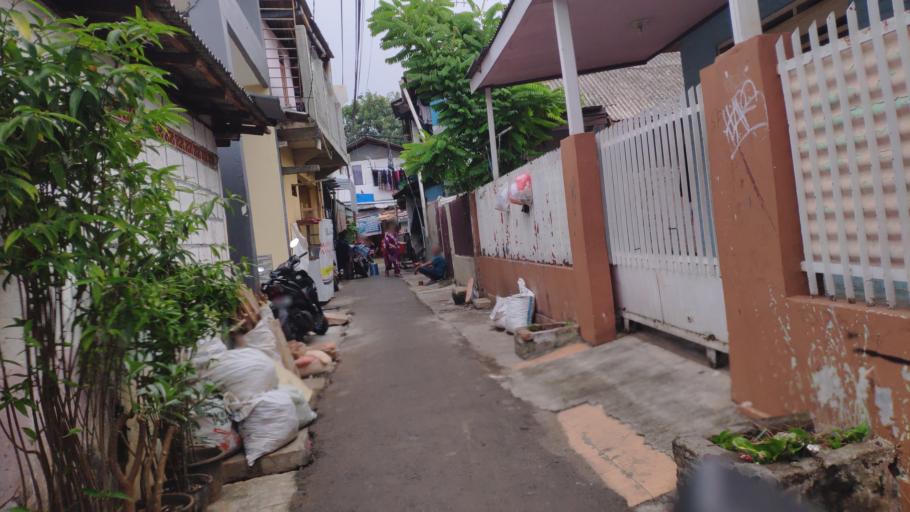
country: ID
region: Jakarta Raya
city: Jakarta
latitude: -6.2190
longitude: 106.8401
